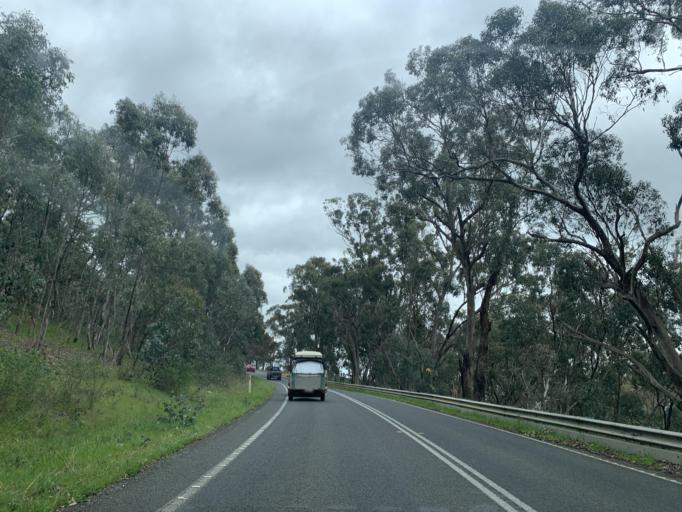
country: AU
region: Victoria
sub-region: Murrindindi
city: Kinglake West
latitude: -37.2071
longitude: 145.0811
